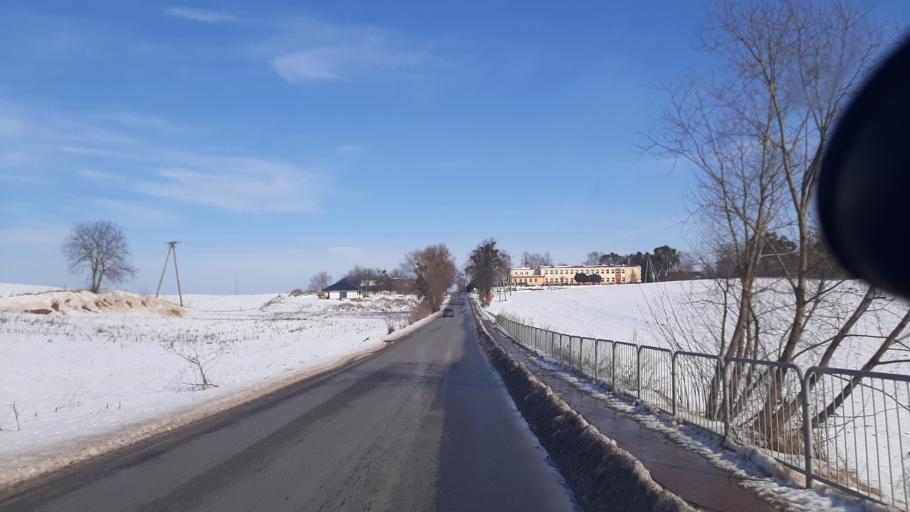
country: PL
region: Lublin Voivodeship
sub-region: Powiat pulawski
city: Kurow
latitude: 51.3572
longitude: 22.1328
